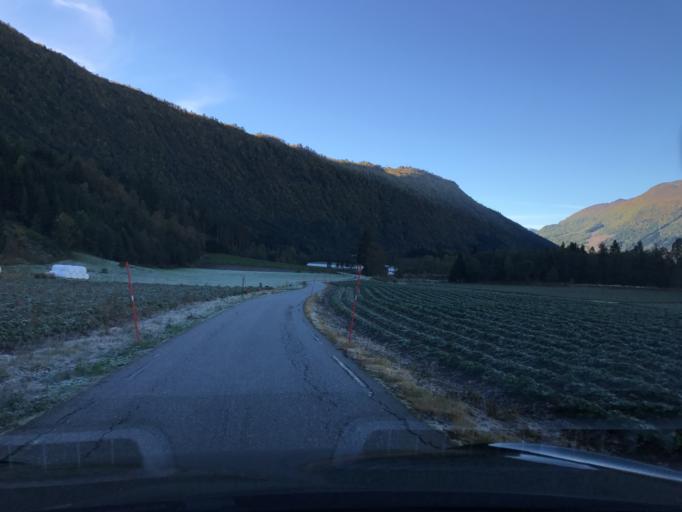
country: NO
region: More og Romsdal
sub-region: Norddal
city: Valldal
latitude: 62.3223
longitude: 7.3289
